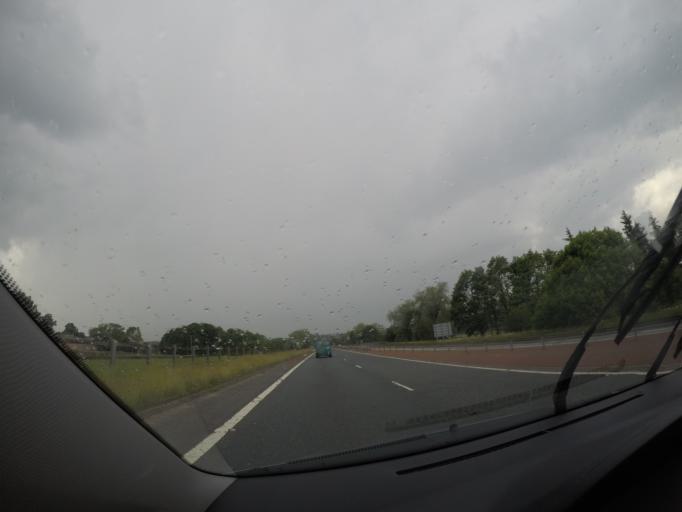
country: GB
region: England
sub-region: Cumbria
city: Penrith
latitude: 54.6546
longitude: -2.7133
